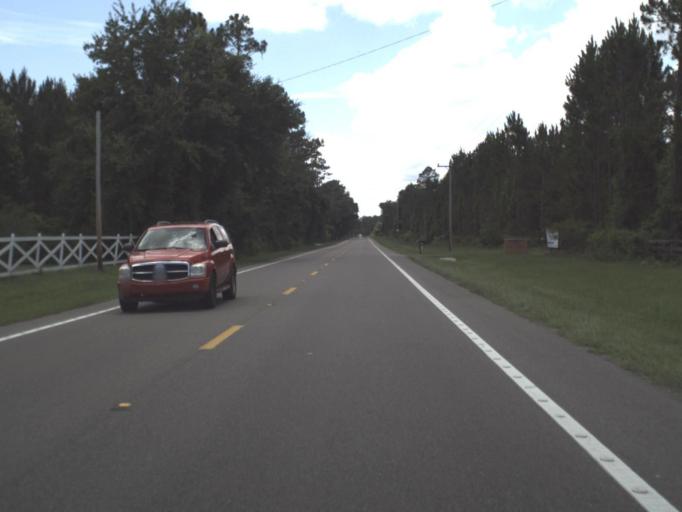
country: US
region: Florida
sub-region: Alachua County
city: Waldo
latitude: 29.7070
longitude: -82.1637
